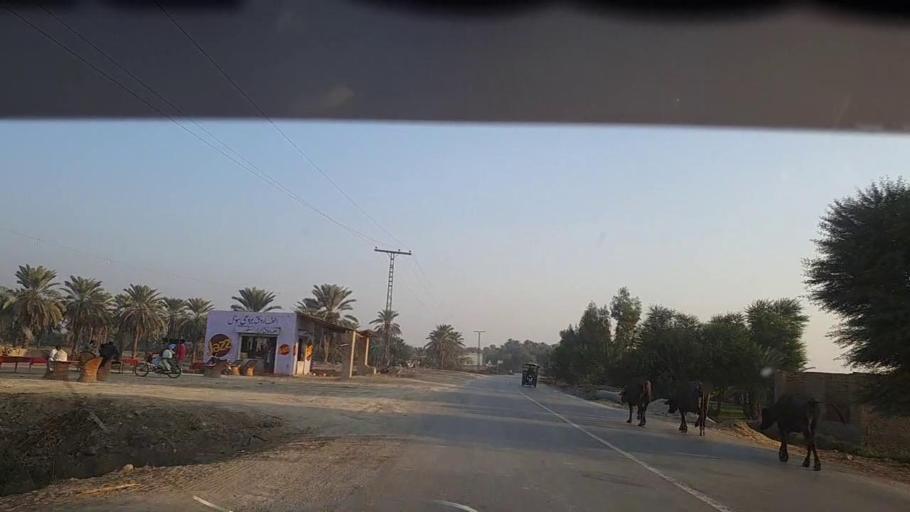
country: PK
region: Sindh
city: Ranipur
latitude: 27.2628
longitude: 68.5243
